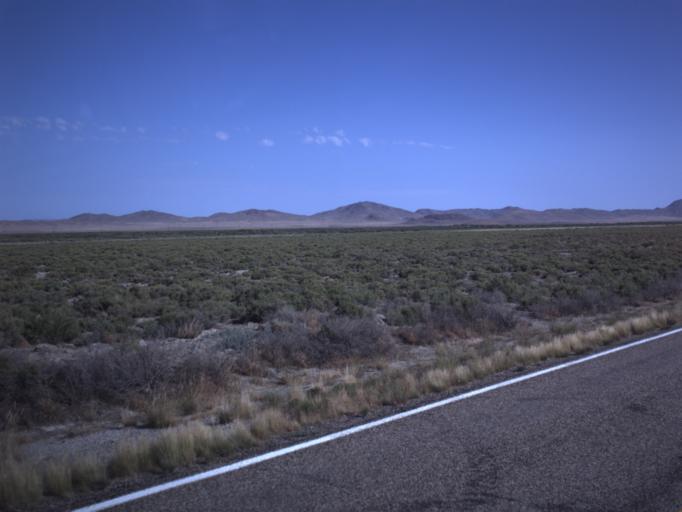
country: US
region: Utah
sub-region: Beaver County
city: Milford
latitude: 38.6262
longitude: -112.9846
